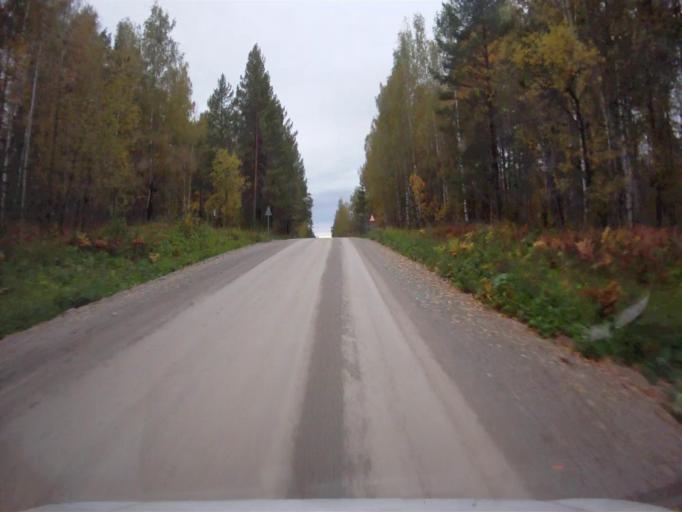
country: RU
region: Chelyabinsk
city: Nyazepetrovsk
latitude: 56.0702
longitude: 59.4313
